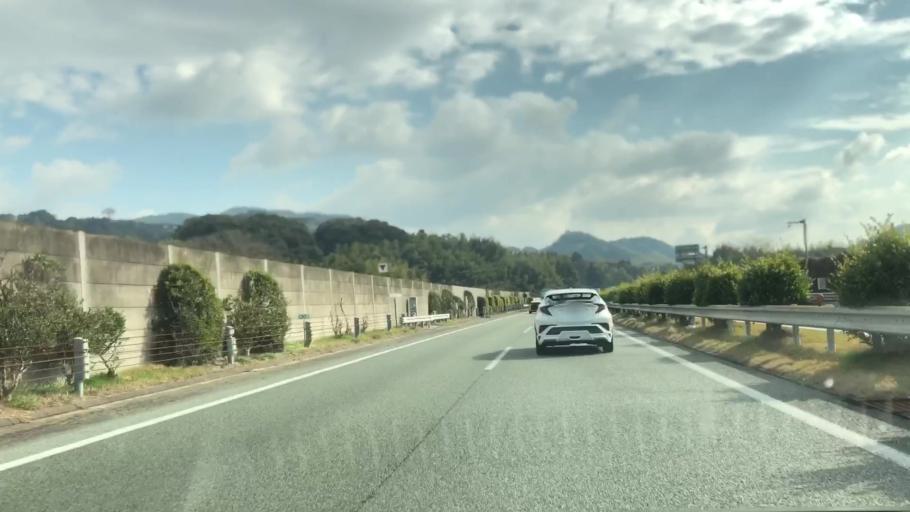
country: JP
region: Fukuoka
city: Setakamachi-takayanagi
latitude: 33.1139
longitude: 130.5297
